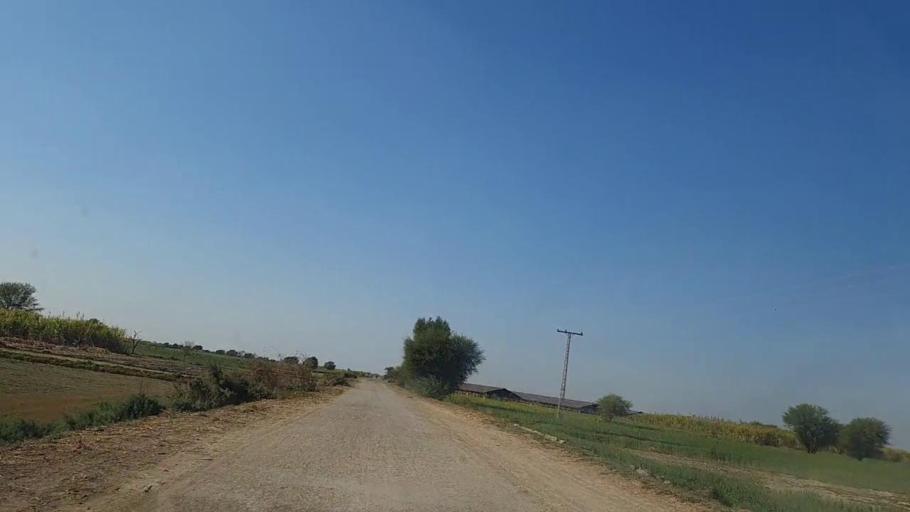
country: PK
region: Sindh
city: Digri
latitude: 25.1649
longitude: 69.0257
